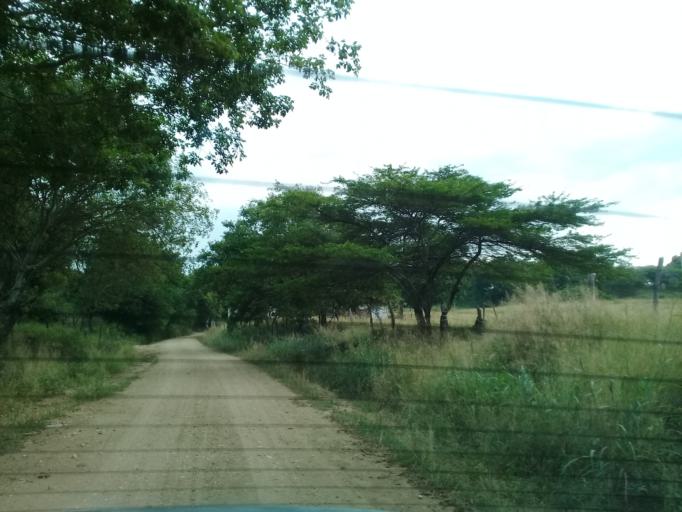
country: CO
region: Cundinamarca
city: Agua de Dios
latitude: 4.3652
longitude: -74.7219
